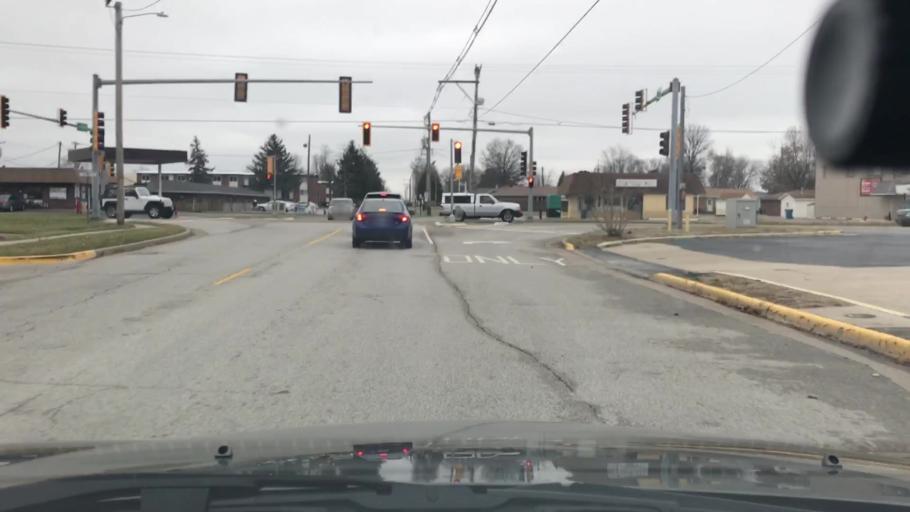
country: US
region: Illinois
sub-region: Madison County
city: Bethalto
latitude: 38.9017
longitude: -90.0406
